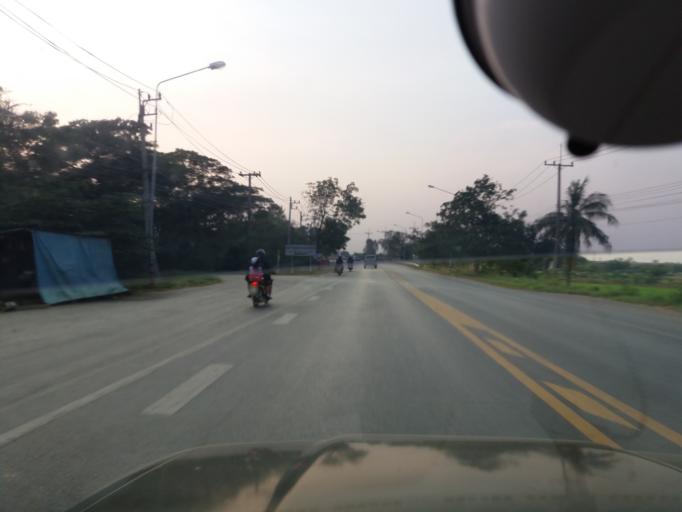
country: TH
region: Sing Buri
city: Sing Buri
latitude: 14.8861
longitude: 100.3735
